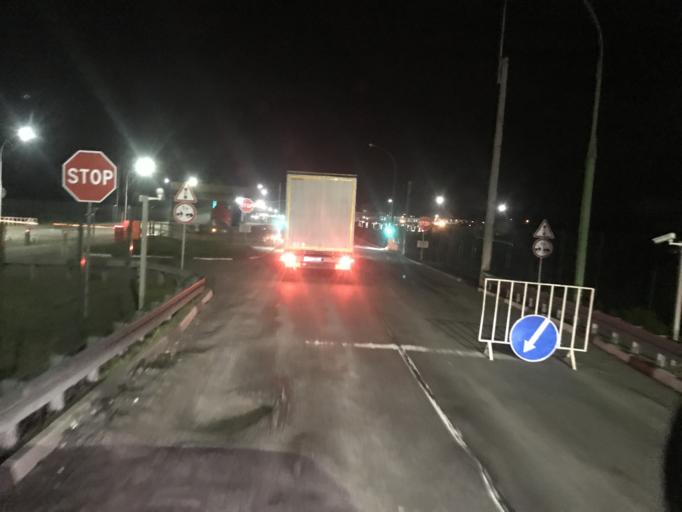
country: PL
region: Lublin Voivodeship
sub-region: Powiat bialski
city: Terespol
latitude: 52.1176
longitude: 23.5675
